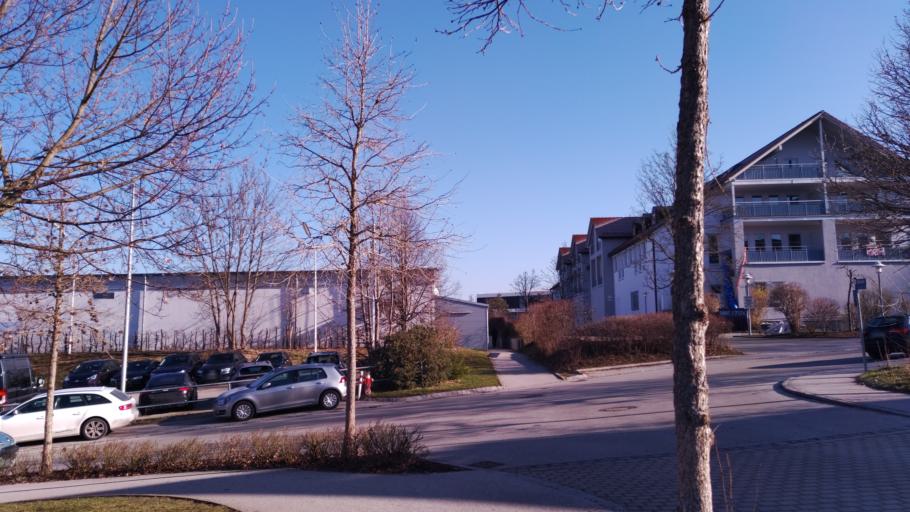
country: DE
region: Bavaria
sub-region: Upper Bavaria
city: Weilheim
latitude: 47.8466
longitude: 11.1517
